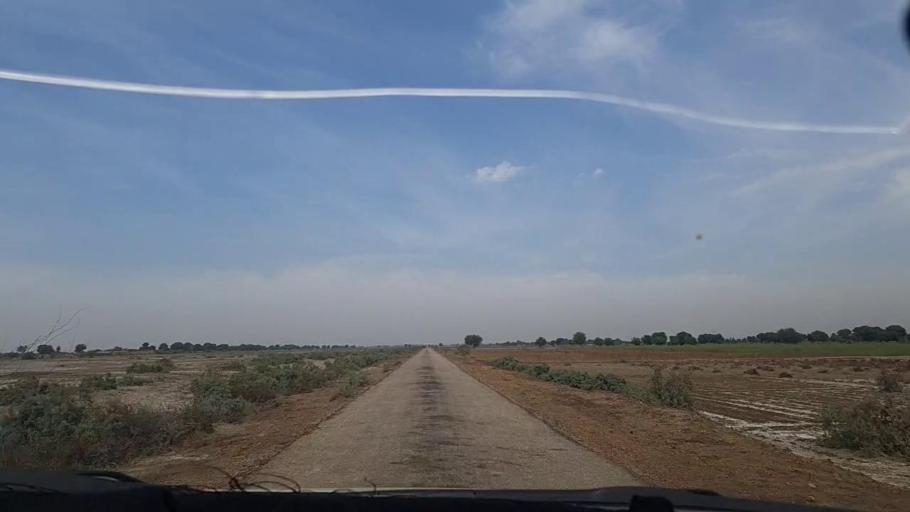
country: PK
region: Sindh
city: Pithoro
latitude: 25.4598
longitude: 69.4699
